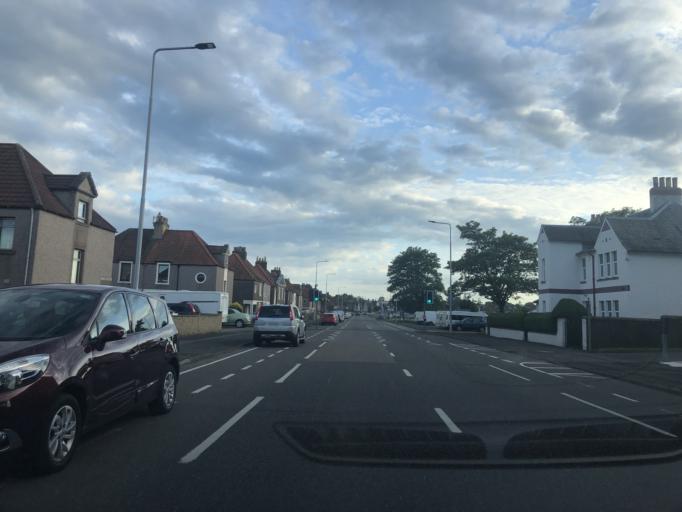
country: GB
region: Scotland
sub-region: Fife
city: Buckhaven
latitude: 56.1766
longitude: -3.0272
